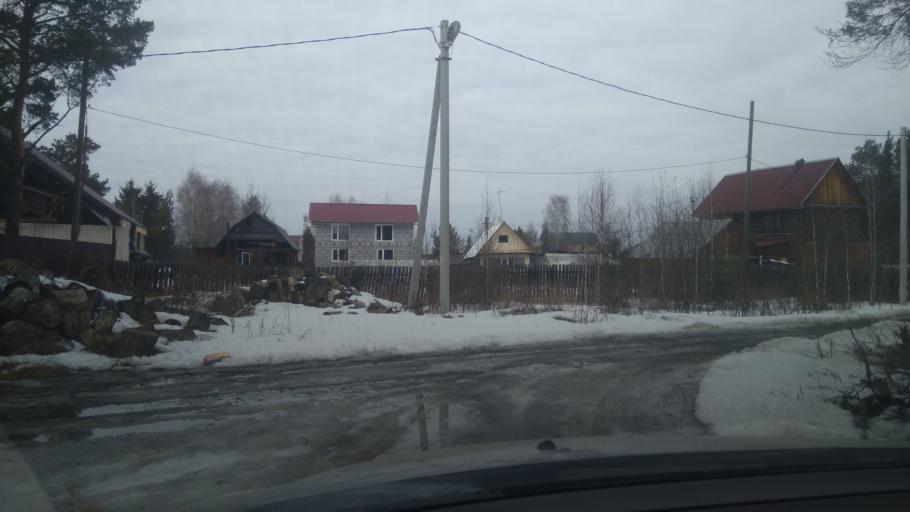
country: RU
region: Sverdlovsk
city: Severka
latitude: 56.8531
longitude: 60.3786
